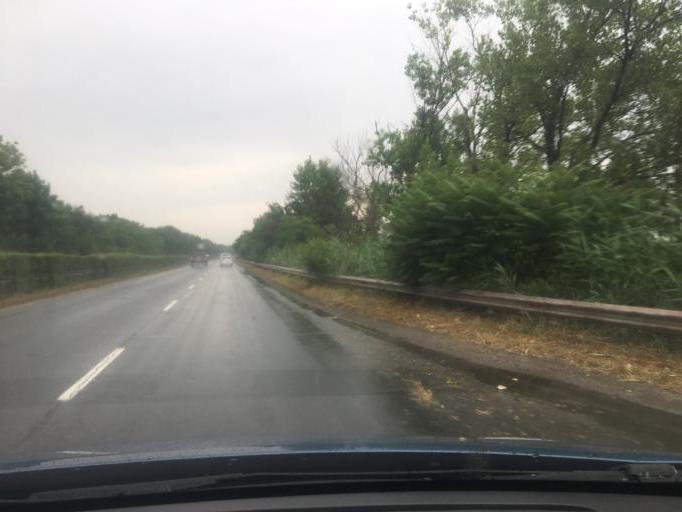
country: BG
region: Burgas
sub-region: Obshtina Burgas
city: Burgas
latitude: 42.5385
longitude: 27.4720
